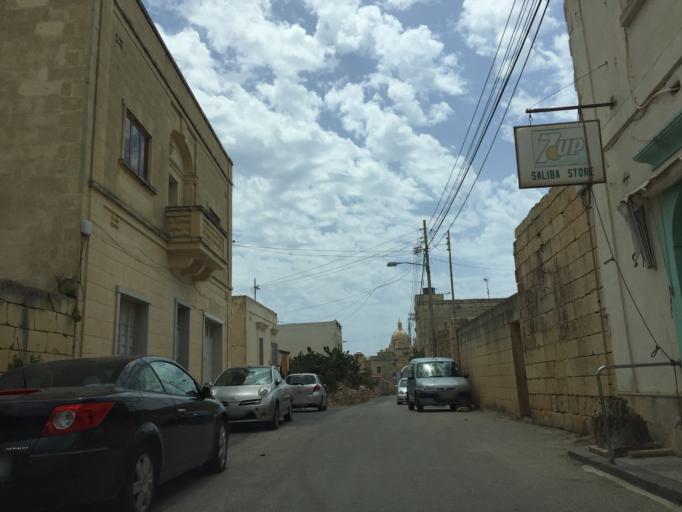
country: MT
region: Iz-Zebbug
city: Zebbug
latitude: 36.0729
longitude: 14.2367
